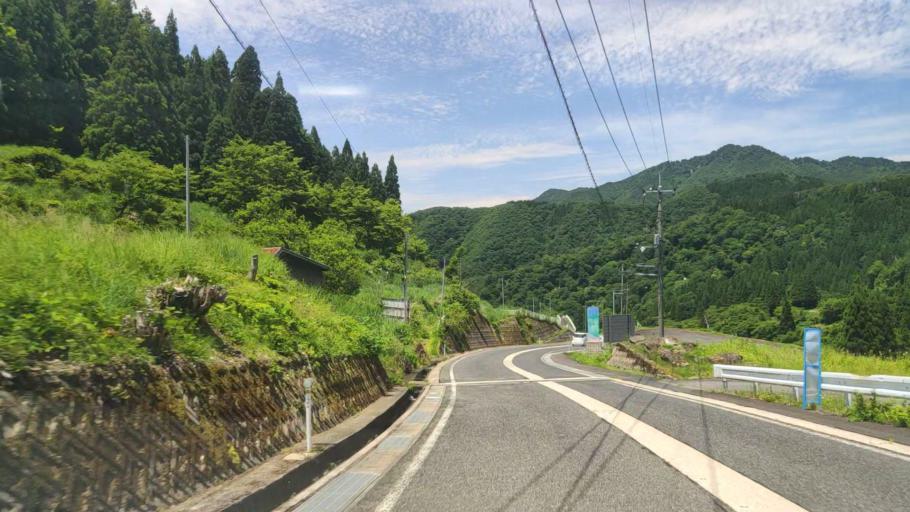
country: JP
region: Tottori
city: Tottori
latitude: 35.3555
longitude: 134.4853
